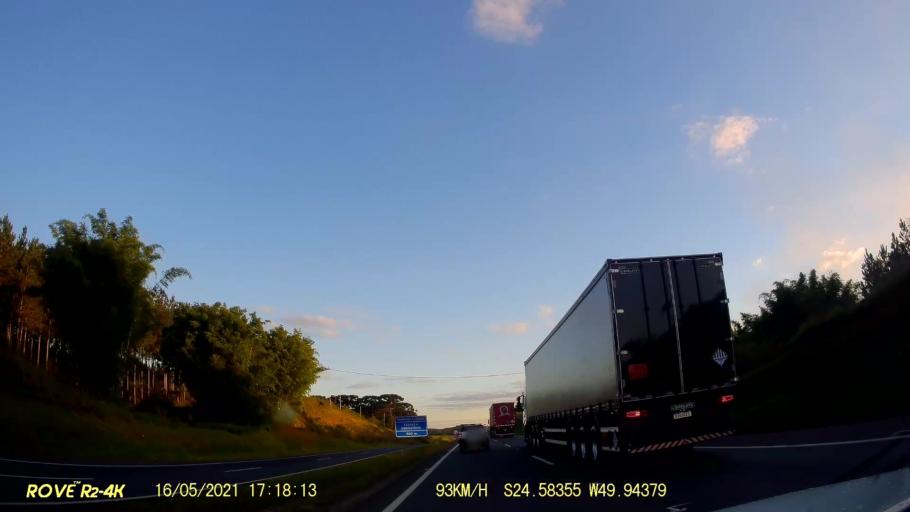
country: BR
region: Parana
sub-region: Pirai Do Sul
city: Pirai do Sul
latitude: -24.5839
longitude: -49.9439
